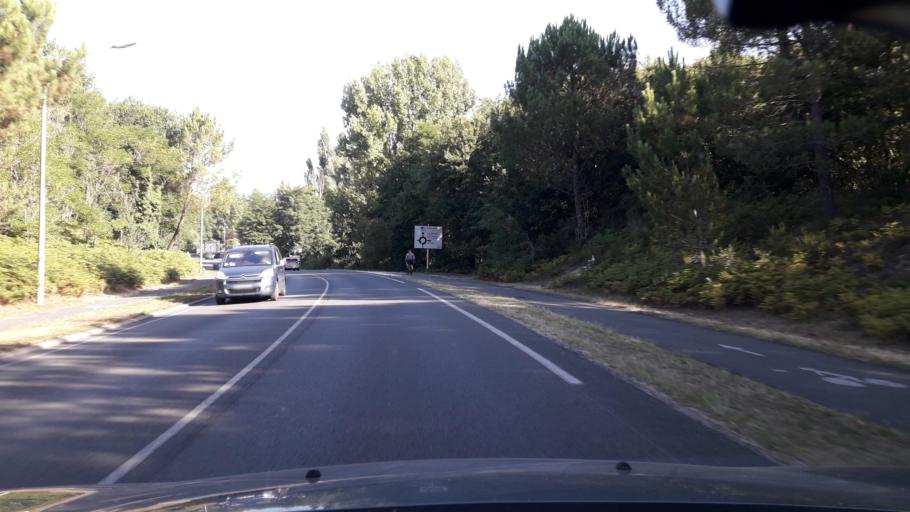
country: FR
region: Poitou-Charentes
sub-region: Departement de la Charente-Maritime
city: Les Mathes
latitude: 45.7106
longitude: -1.1592
